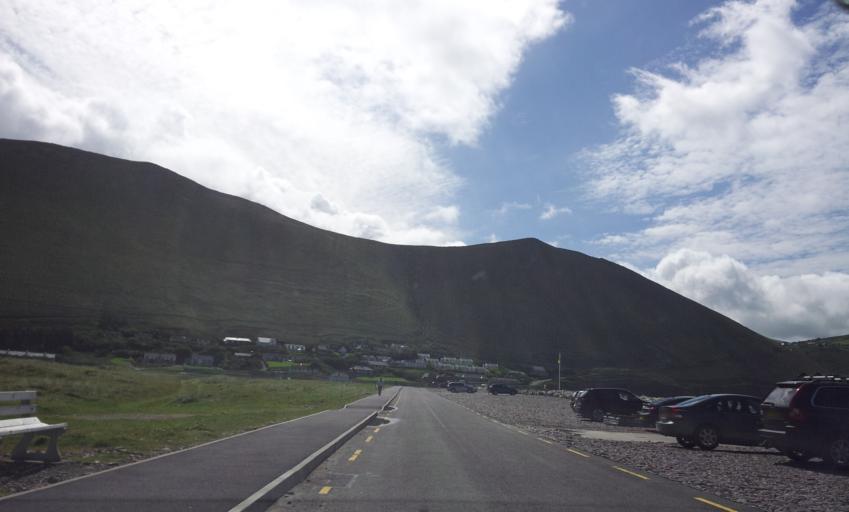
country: IE
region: Munster
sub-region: Ciarrai
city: Killorglin
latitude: 52.0590
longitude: -9.9744
